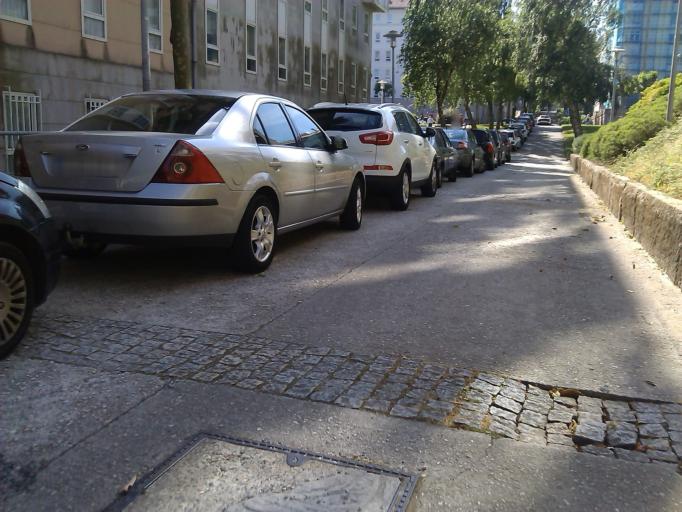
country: ES
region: Galicia
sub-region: Provincia da Coruna
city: Santiago de Compostela
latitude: 42.8820
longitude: -8.5289
